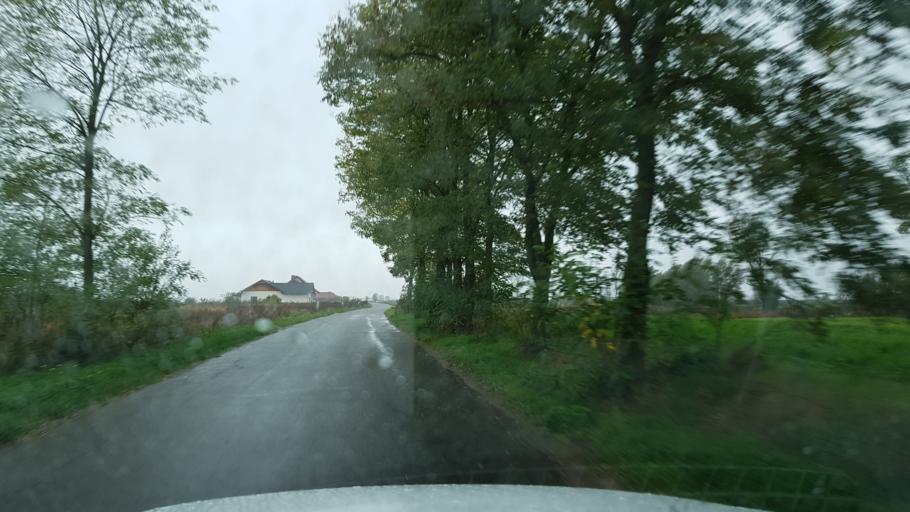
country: PL
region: West Pomeranian Voivodeship
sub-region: Powiat pyrzycki
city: Kozielice
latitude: 53.1621
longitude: 14.8371
